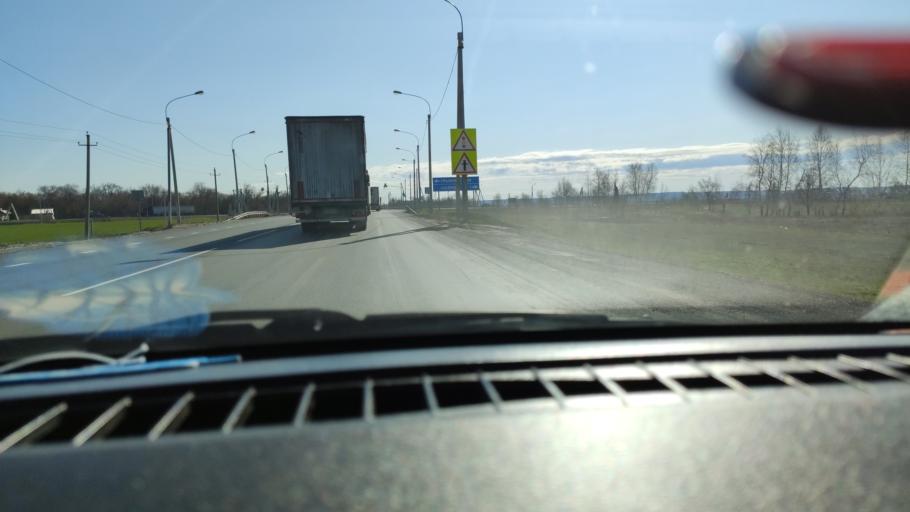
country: RU
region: Samara
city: Syzran'
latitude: 53.2096
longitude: 48.5067
